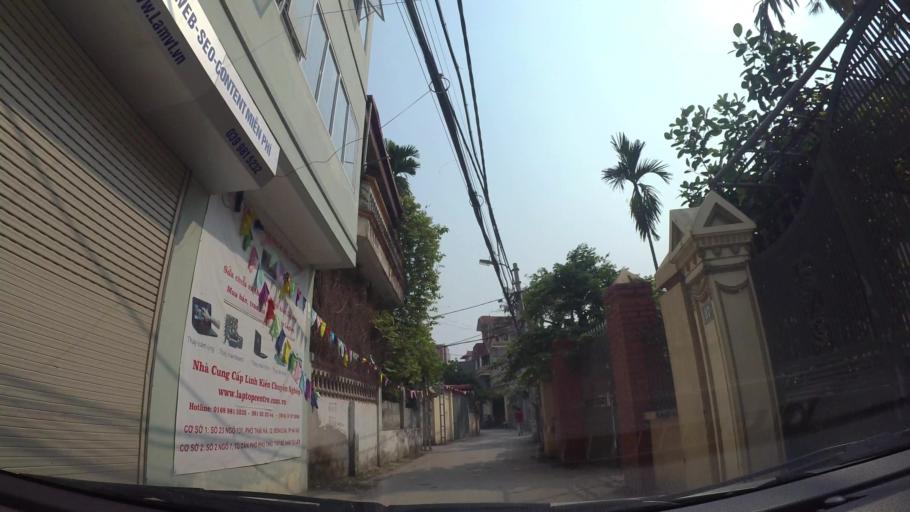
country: VN
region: Ha Noi
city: Cau Dien
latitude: 21.0036
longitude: 105.7513
